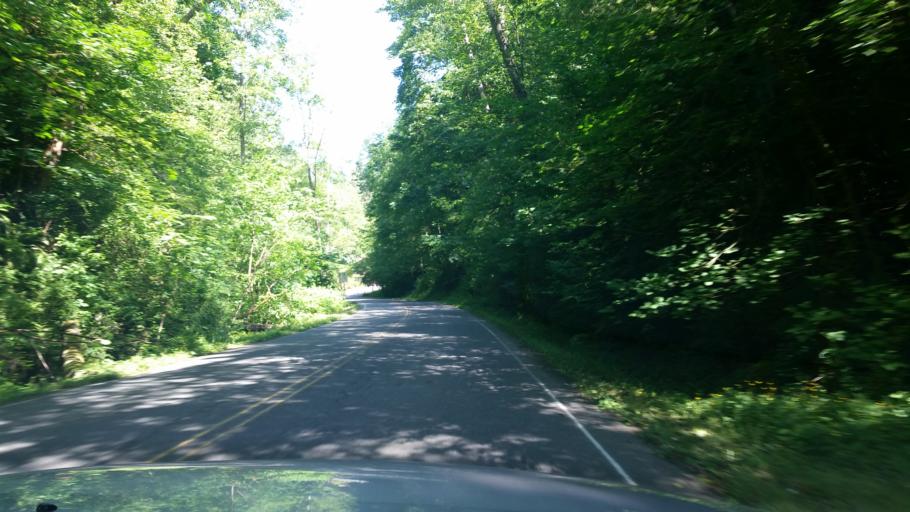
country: US
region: Washington
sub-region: King County
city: Lake Forest Park
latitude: 47.7595
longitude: -122.2972
